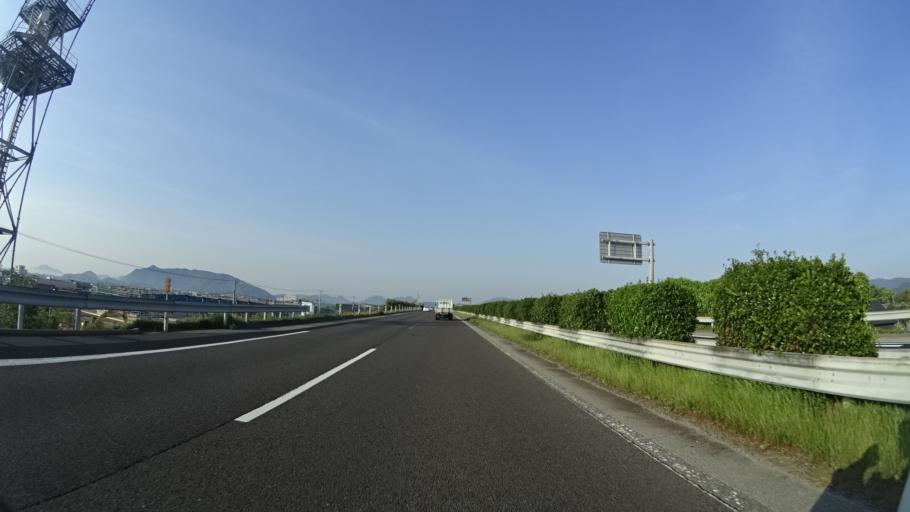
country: JP
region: Kagawa
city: Kan'onjicho
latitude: 34.0881
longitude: 133.6579
